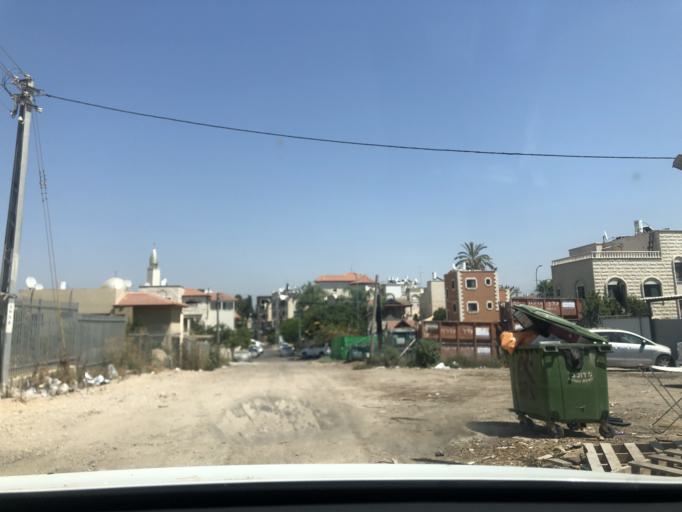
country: IL
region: Central District
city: Lod
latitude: 31.9580
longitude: 34.9007
